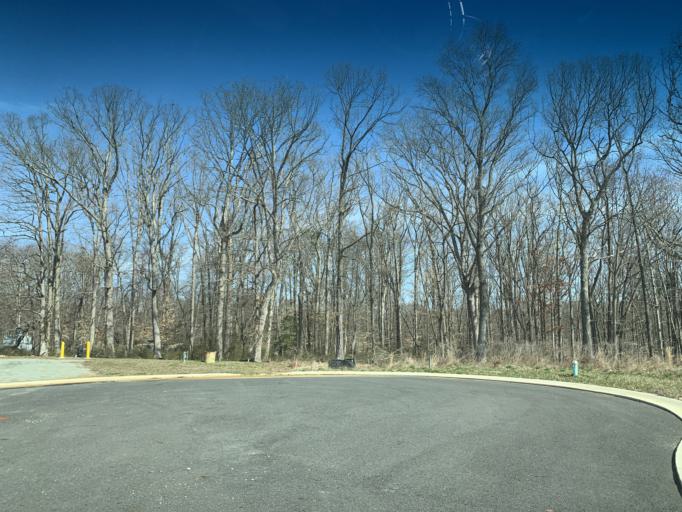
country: US
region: Maryland
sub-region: Cecil County
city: Charlestown
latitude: 39.5562
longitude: -76.0108
